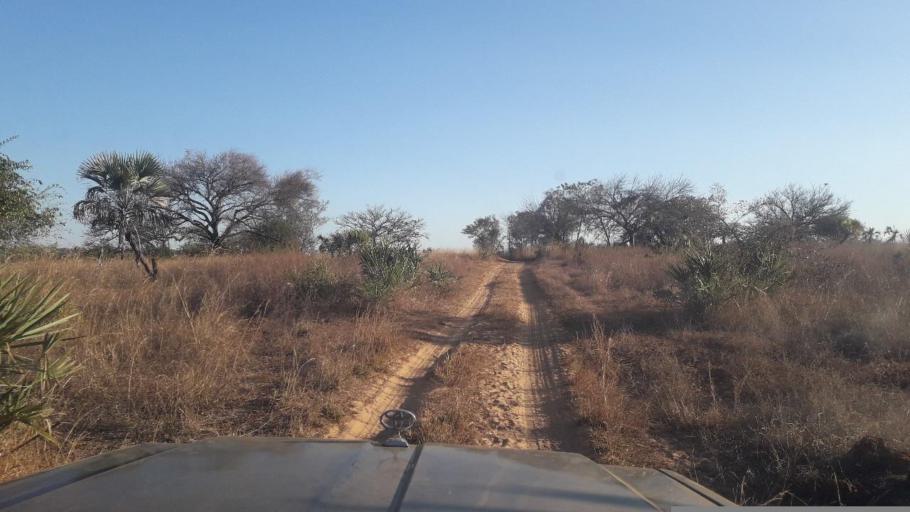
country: MG
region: Boeny
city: Sitampiky
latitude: -16.5025
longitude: 45.6024
